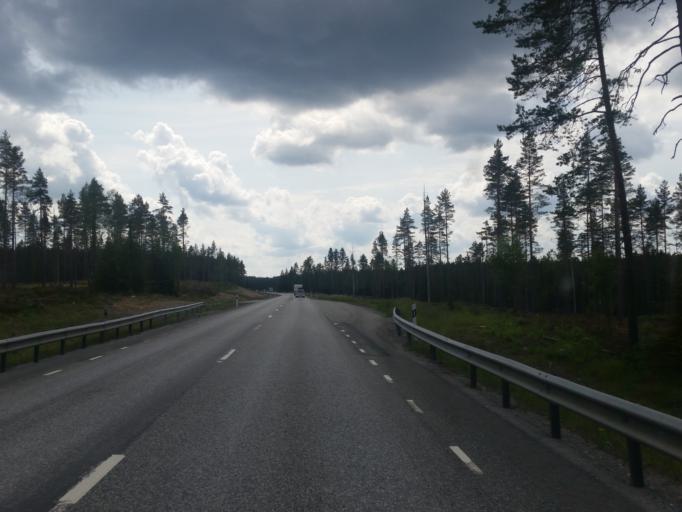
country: SE
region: OErebro
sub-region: Ljusnarsbergs Kommun
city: Kopparberg
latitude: 59.9541
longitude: 15.0206
